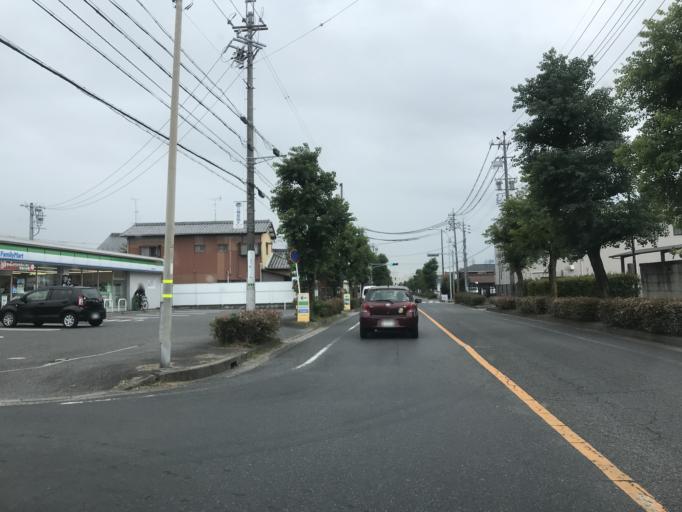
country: JP
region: Aichi
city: Nagoya-shi
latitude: 35.2048
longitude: 136.8397
